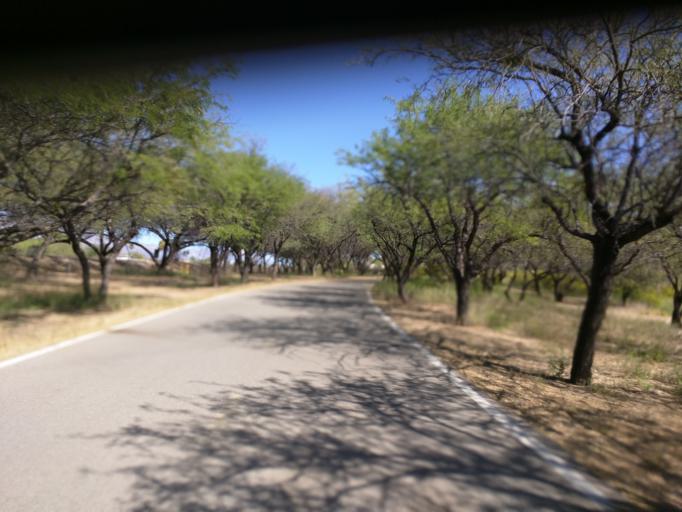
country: US
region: Arizona
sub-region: Pima County
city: Flowing Wells
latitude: 32.2971
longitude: -111.0008
